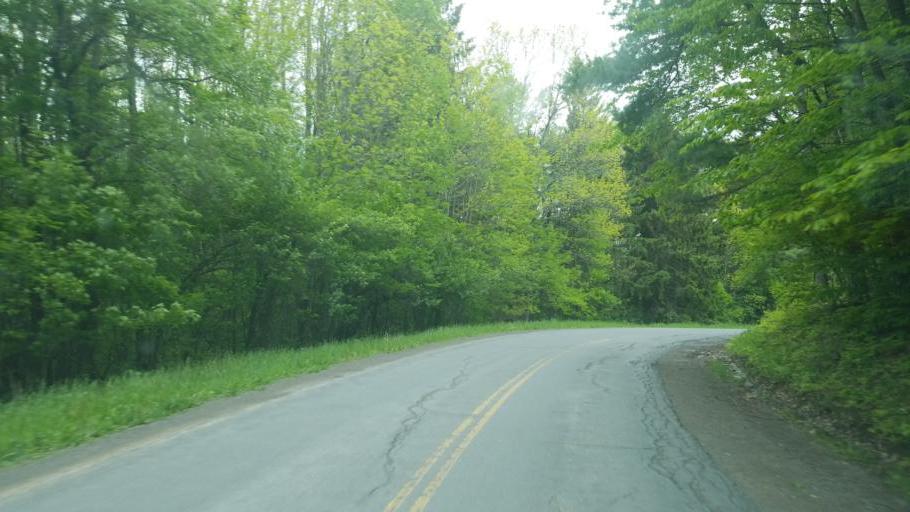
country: US
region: New York
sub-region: Otsego County
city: Richfield Springs
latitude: 42.8271
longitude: -74.9559
